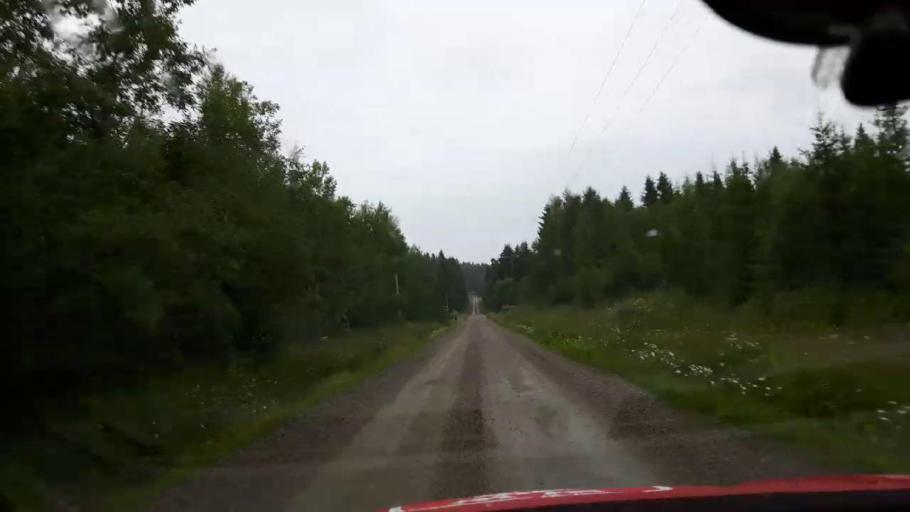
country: SE
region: Jaemtland
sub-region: OEstersunds Kommun
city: Brunflo
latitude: 62.7815
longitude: 14.9751
